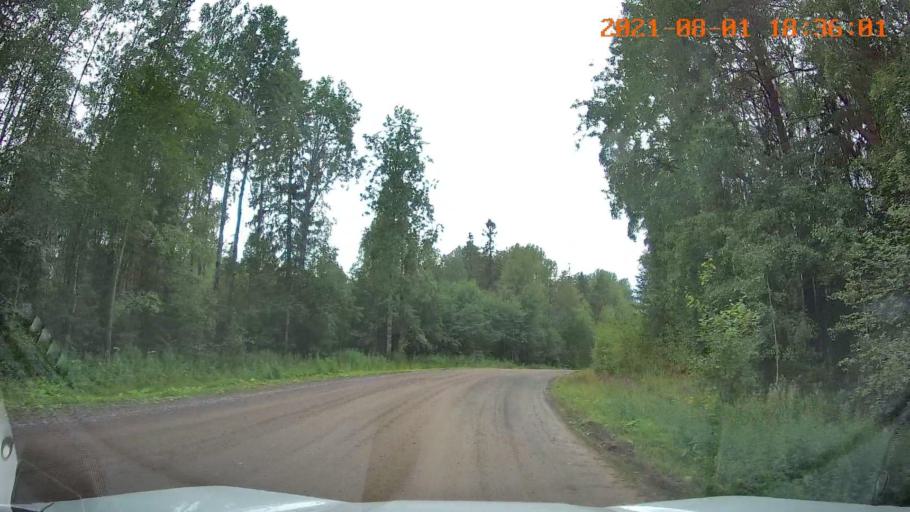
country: RU
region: Leningrad
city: Voznesen'ye
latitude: 60.9048
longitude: 35.2627
